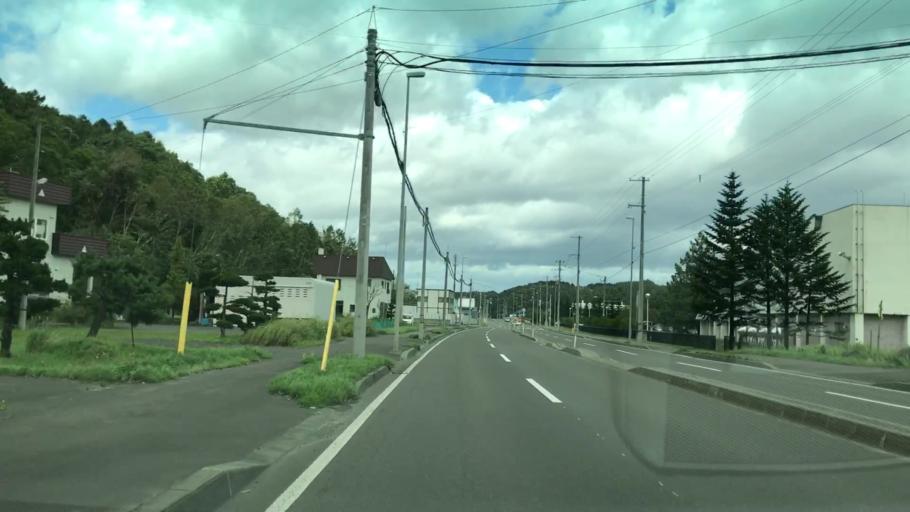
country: JP
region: Hokkaido
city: Kitahiroshima
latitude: 42.9703
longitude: 141.4526
